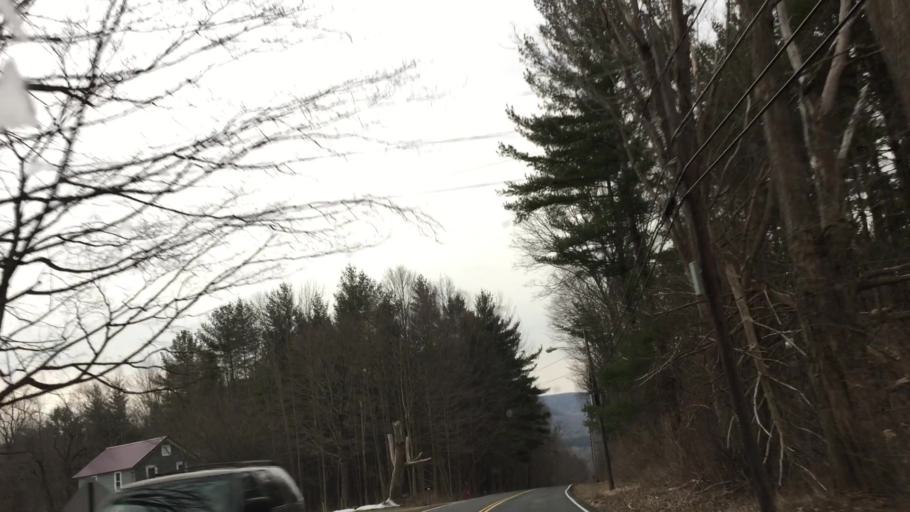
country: US
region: Massachusetts
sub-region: Berkshire County
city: Lee
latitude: 42.3386
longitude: -73.2540
